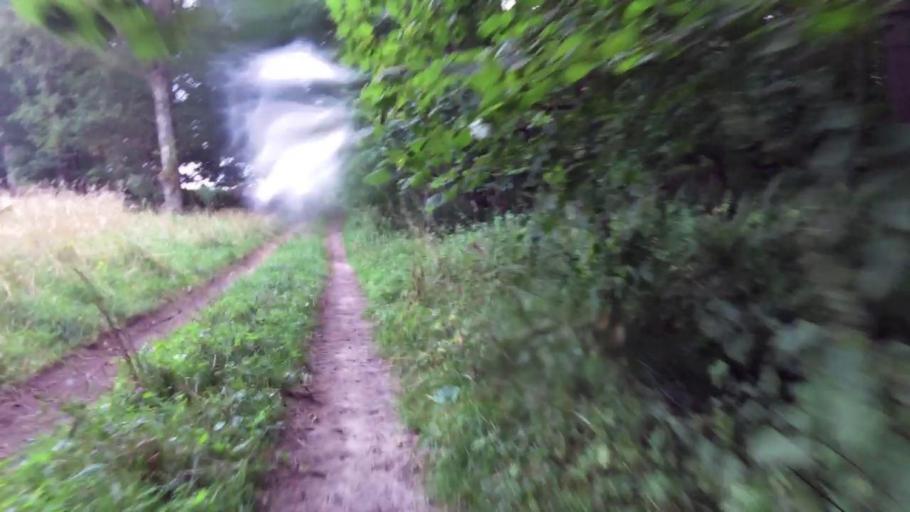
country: PL
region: West Pomeranian Voivodeship
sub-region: Powiat drawski
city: Drawsko Pomorskie
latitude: 53.5402
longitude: 15.7075
